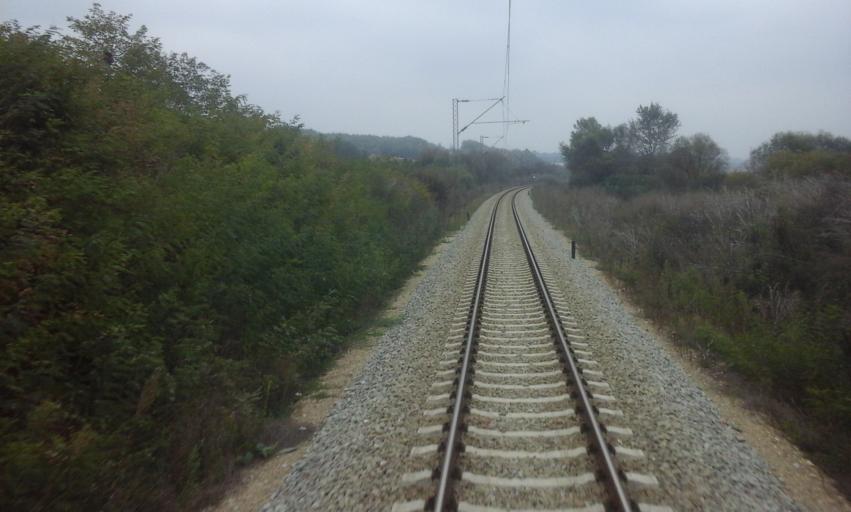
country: RS
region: Central Serbia
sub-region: Belgrade
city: Sopot
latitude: 44.5000
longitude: 20.6444
